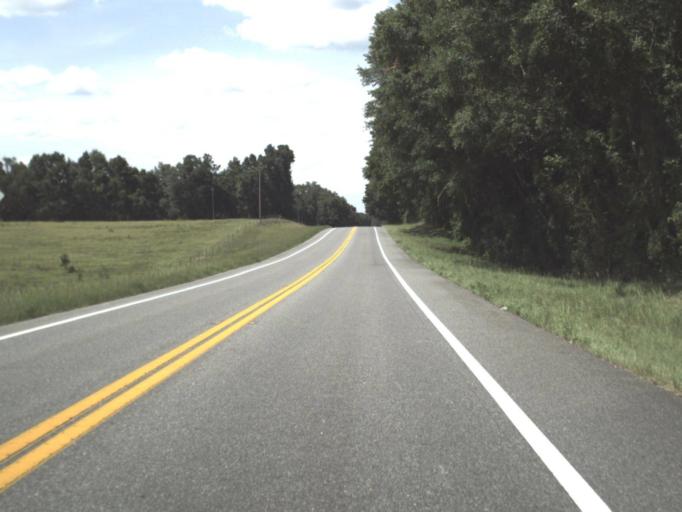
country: US
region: Florida
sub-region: Gilchrist County
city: Trenton
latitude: 29.7296
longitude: -82.7449
